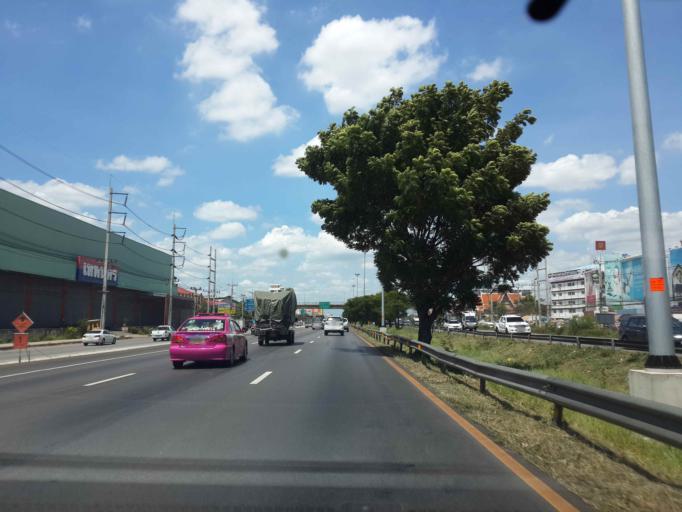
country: TH
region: Bangkok
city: Bang Bon
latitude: 13.5957
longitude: 100.3633
